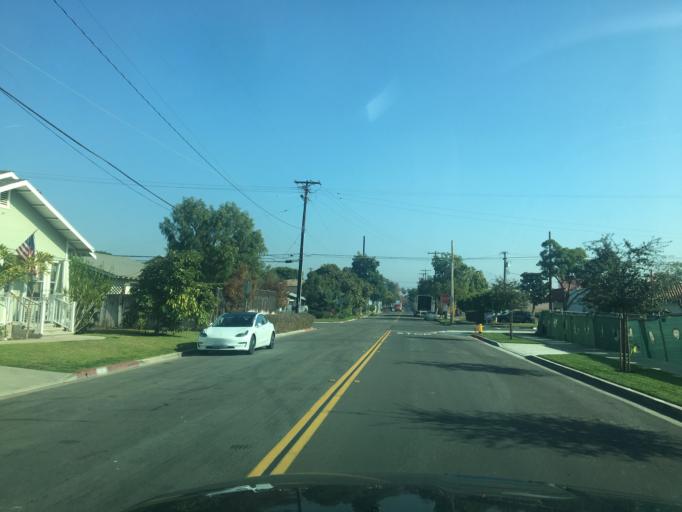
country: US
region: California
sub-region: Orange County
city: Tustin
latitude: 33.7401
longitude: -117.8267
